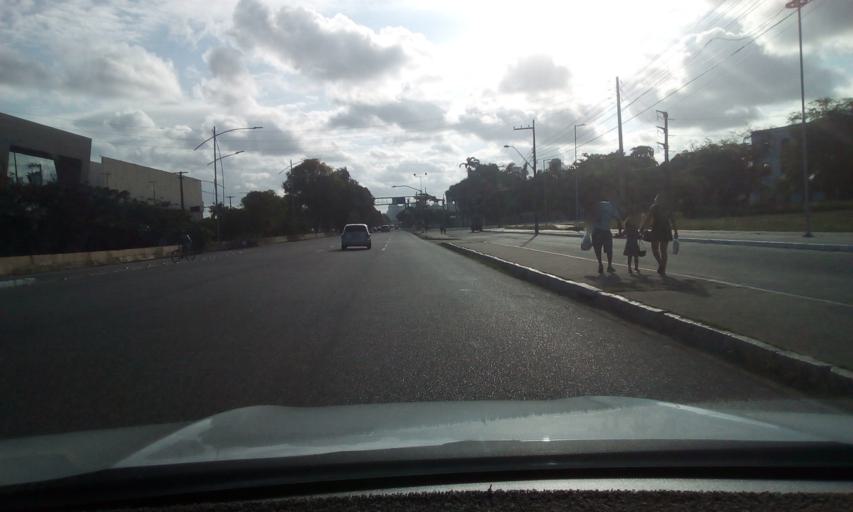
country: BR
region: Pernambuco
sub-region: Recife
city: Recife
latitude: -8.0360
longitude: -34.8714
